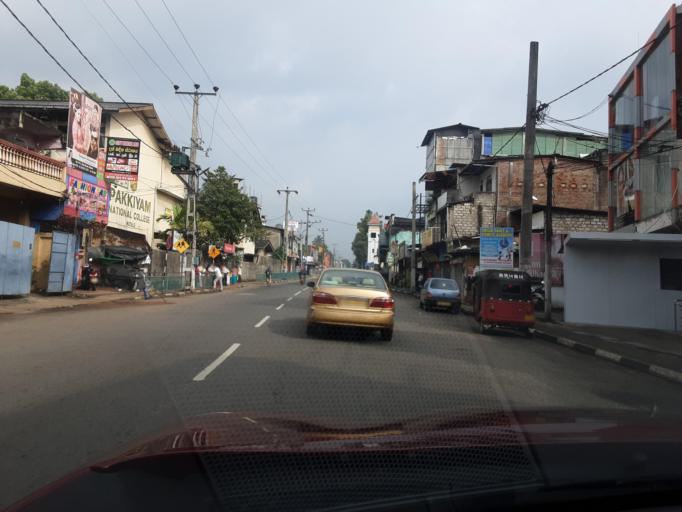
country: LK
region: Central
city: Kandy
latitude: 7.4676
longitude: 80.6228
